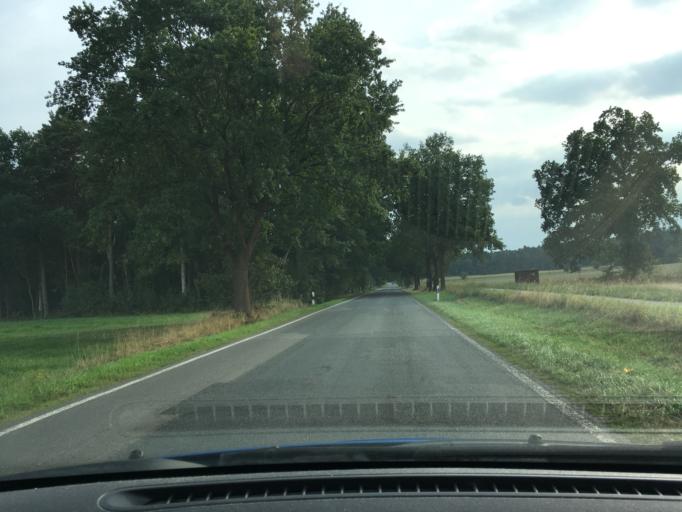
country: DE
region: Lower Saxony
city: Asendorf
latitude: 53.2831
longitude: 9.9762
